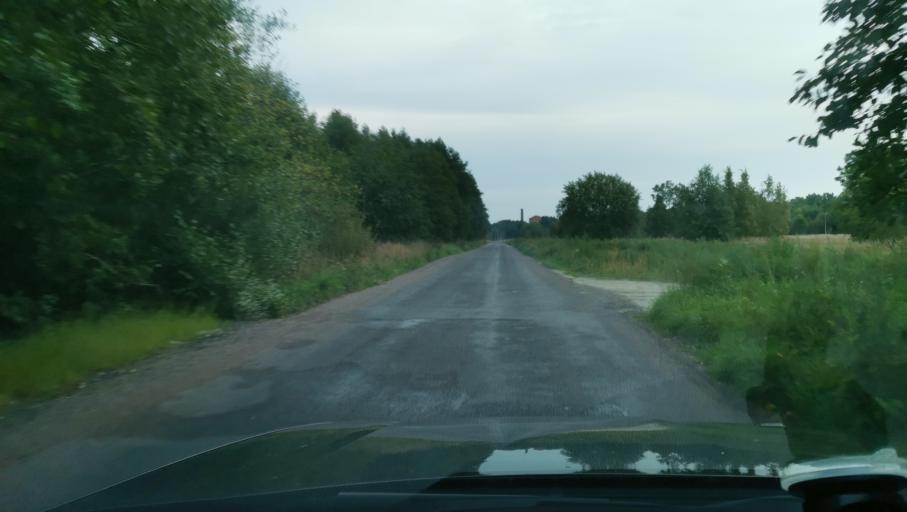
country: EE
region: Harju
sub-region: Saue vald
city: Laagri
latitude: 59.4227
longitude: 24.6258
